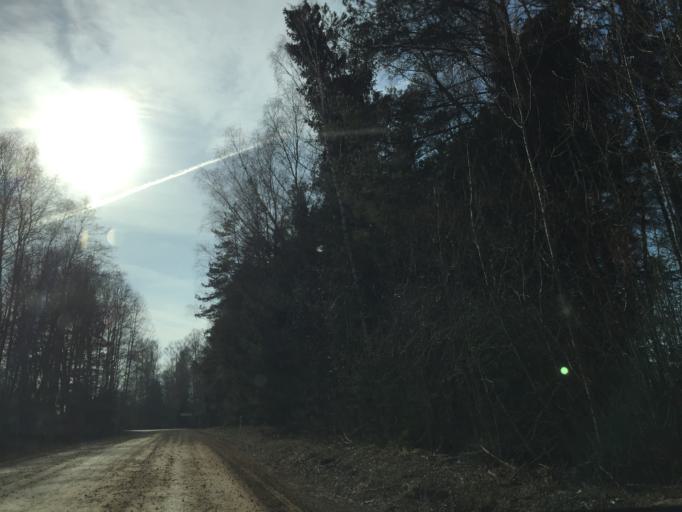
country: LV
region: Saulkrastu
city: Saulkrasti
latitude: 57.2840
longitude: 24.4631
